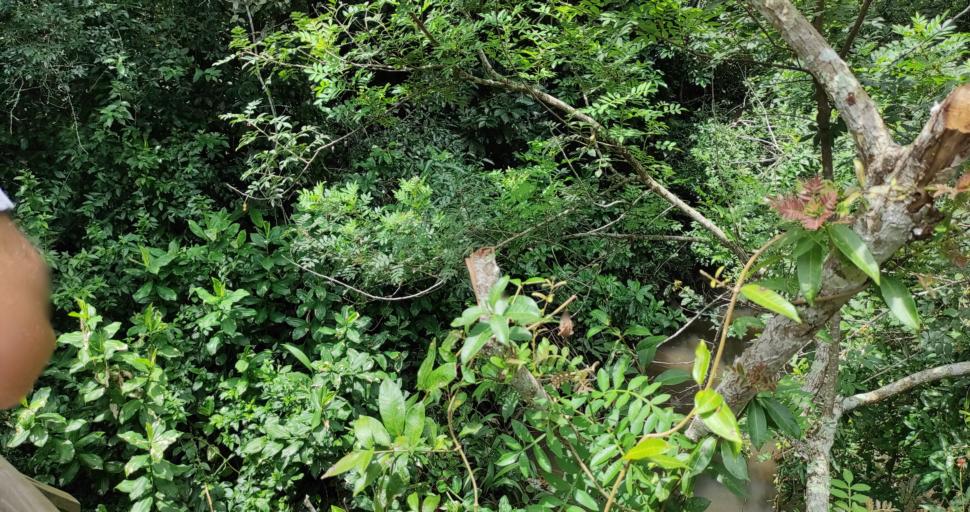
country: AR
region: Misiones
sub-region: Departamento de Iguazu
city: Puerto Iguazu
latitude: -25.6840
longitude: -54.4467
